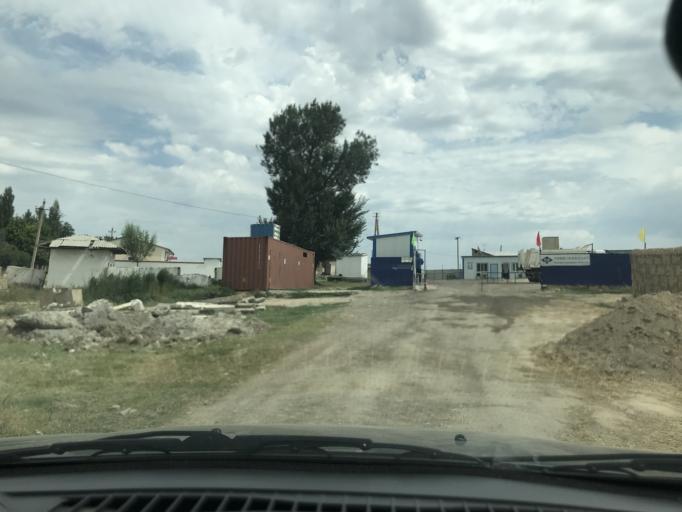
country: UZ
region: Namangan
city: Yangiqo`rg`on
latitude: 41.2209
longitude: 71.6464
